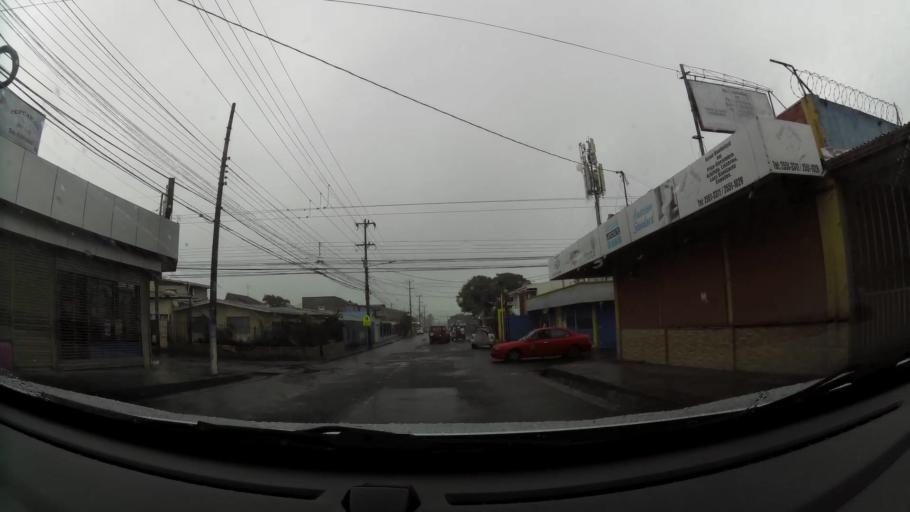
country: CR
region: Cartago
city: Cartago
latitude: 9.8624
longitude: -83.9157
